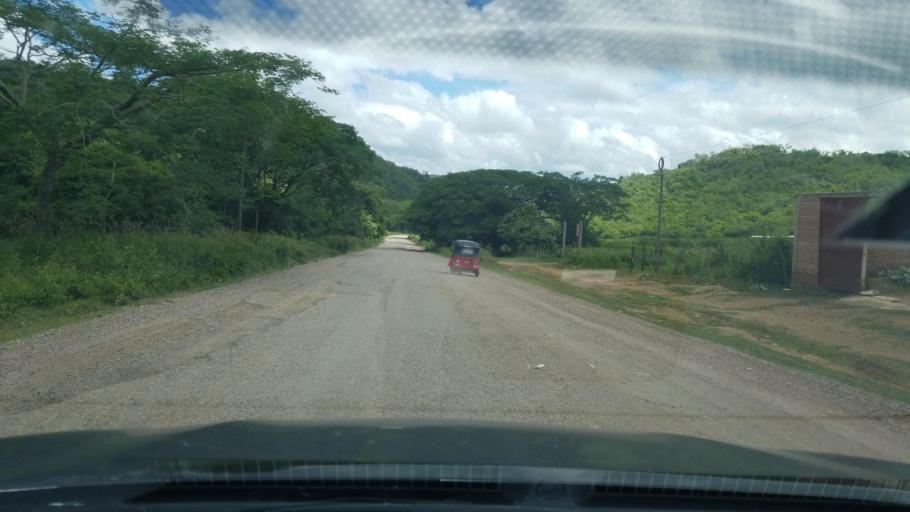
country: HN
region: Francisco Morazan
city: Talanga
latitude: 14.3864
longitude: -87.0723
